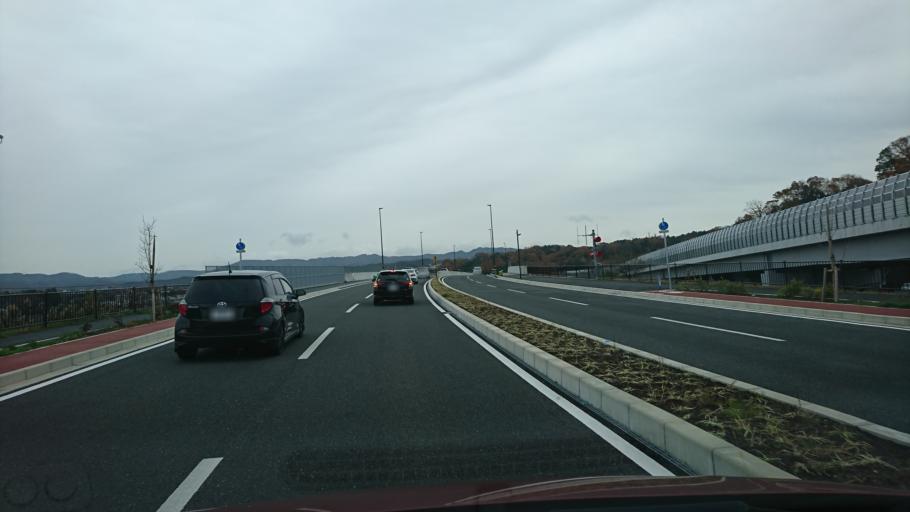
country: JP
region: Osaka
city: Ikeda
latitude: 34.8848
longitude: 135.4022
